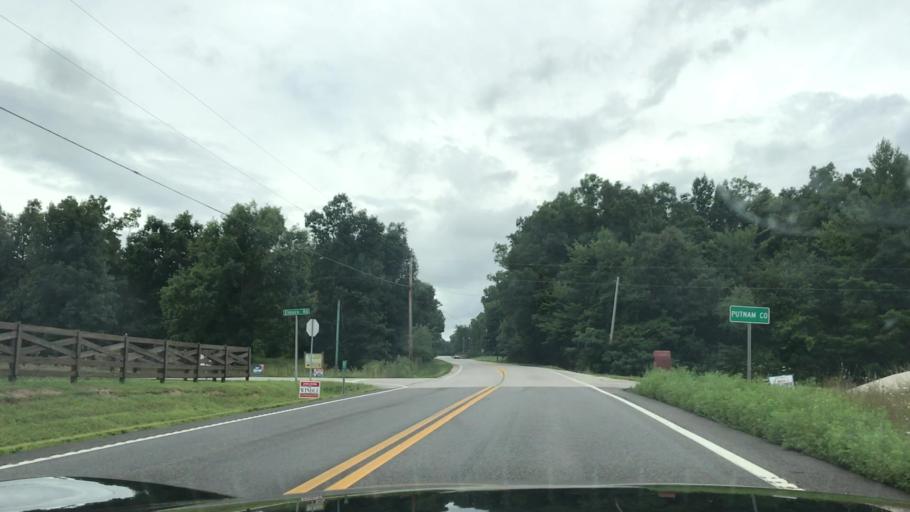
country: US
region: Tennessee
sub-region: Putnam County
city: Monterey
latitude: 36.1395
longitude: -85.1024
